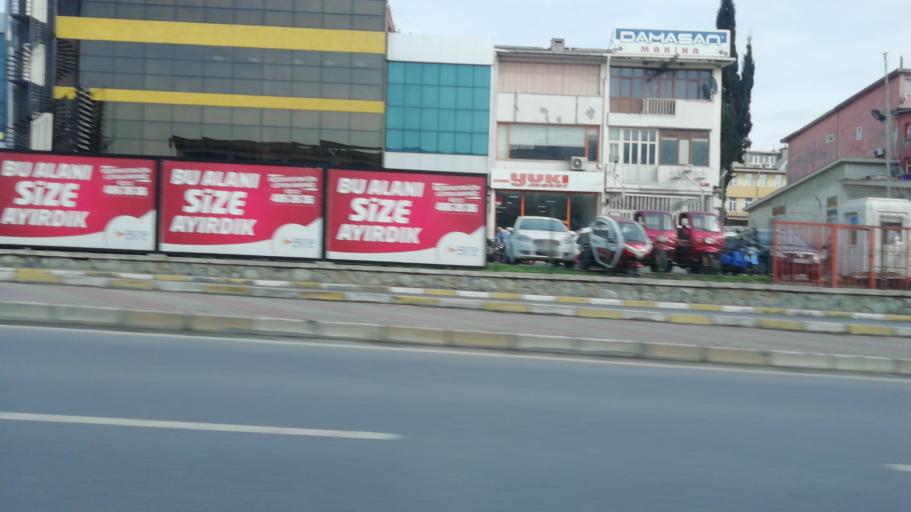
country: TR
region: Istanbul
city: Basaksehir
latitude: 41.0938
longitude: 28.7938
